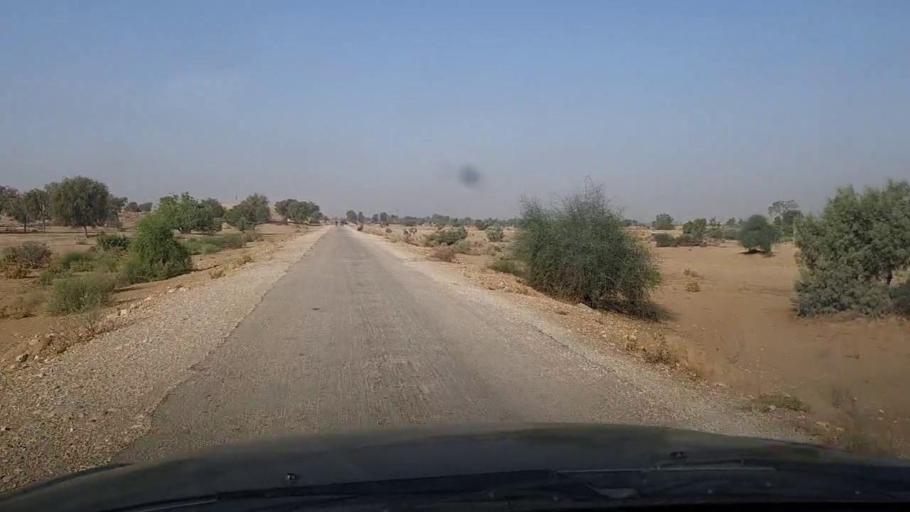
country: PK
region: Sindh
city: Sann
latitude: 26.0240
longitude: 68.1099
